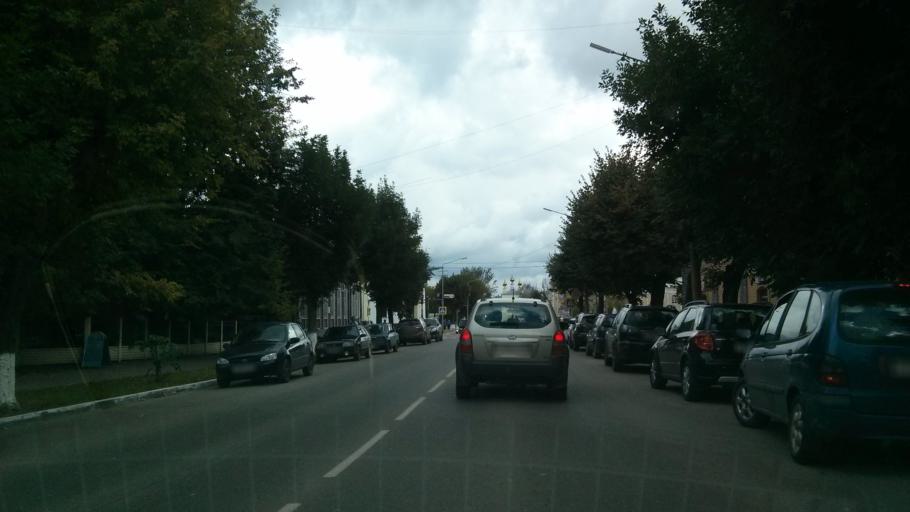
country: RU
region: Vladimir
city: Murom
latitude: 55.5750
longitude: 42.0507
